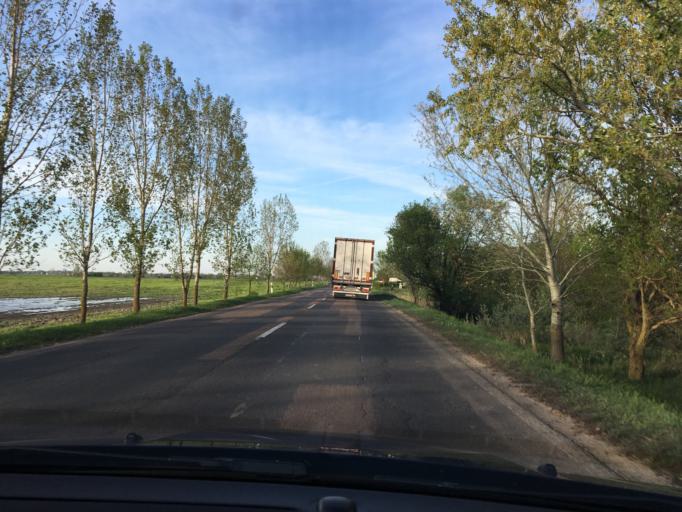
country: HU
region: Hajdu-Bihar
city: Berettyoujfalu
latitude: 47.1761
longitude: 21.5230
